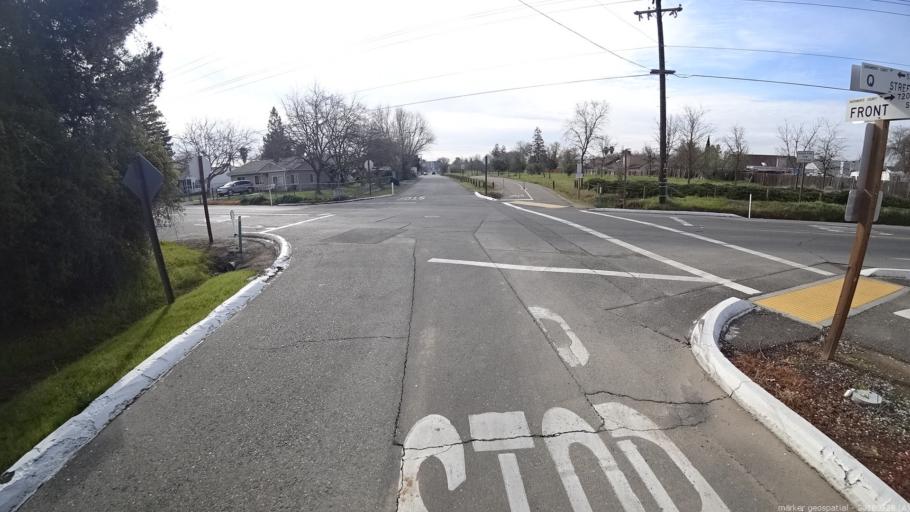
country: US
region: California
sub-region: Sacramento County
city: Rio Linda
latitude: 38.6985
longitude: -121.4534
